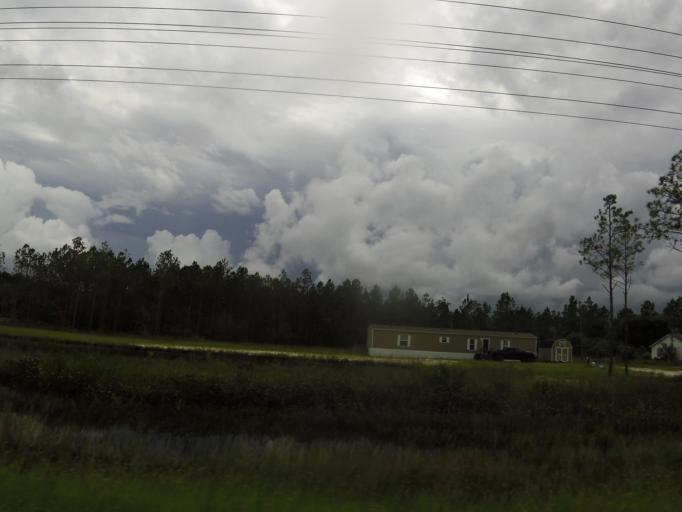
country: US
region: Florida
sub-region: Nassau County
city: Hilliard
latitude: 30.5214
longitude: -82.0562
